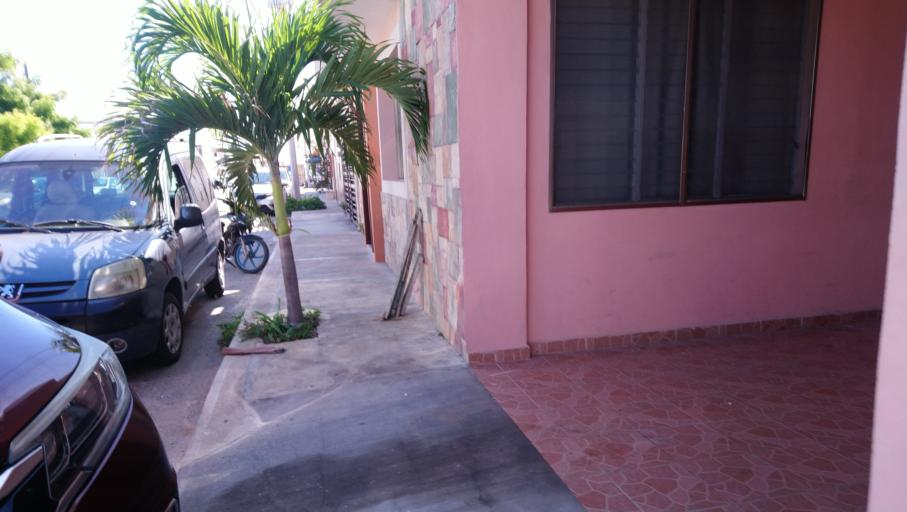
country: MX
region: Yucatan
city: Progreso de Castro
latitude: 21.2840
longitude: -89.6711
